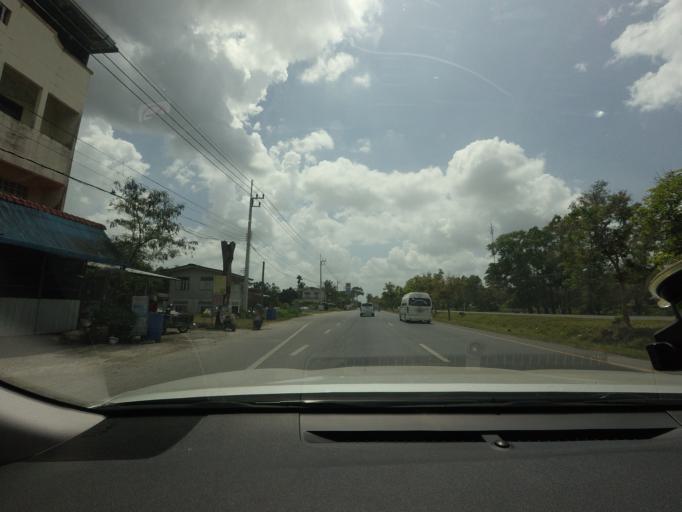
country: TH
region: Nakhon Si Thammarat
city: Nakhon Si Thammarat
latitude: 8.4202
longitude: 99.9213
